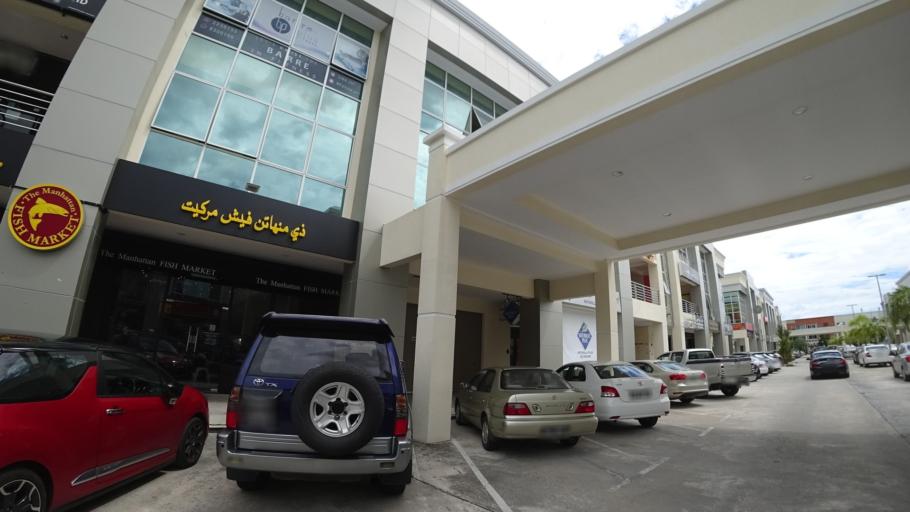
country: BN
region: Brunei and Muara
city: Bandar Seri Begawan
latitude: 4.9048
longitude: 114.9228
